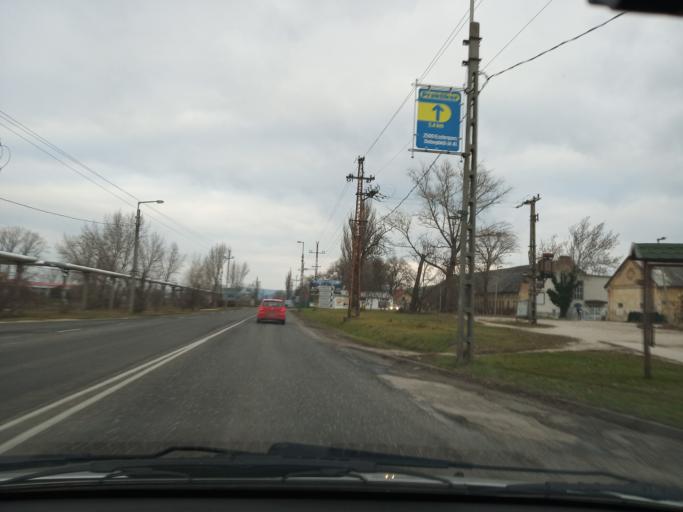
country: HU
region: Komarom-Esztergom
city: Dorog
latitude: 47.7496
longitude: 18.7311
